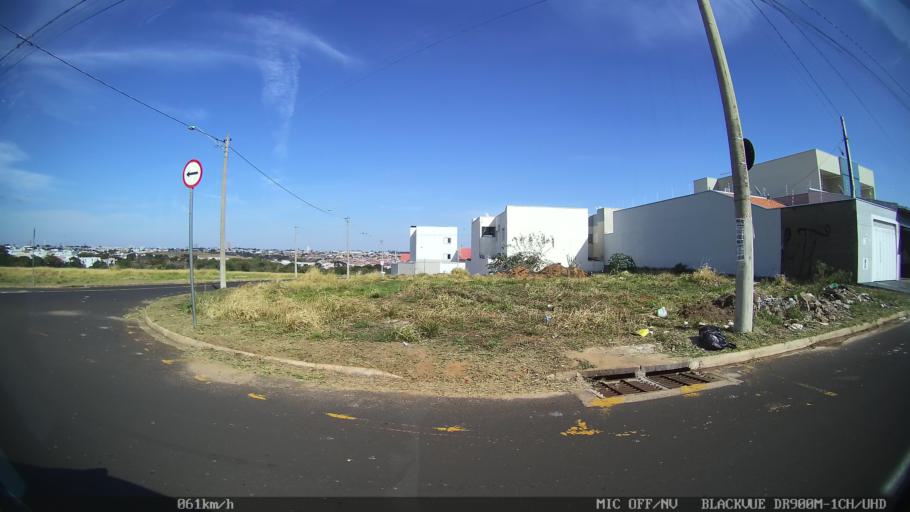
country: BR
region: Sao Paulo
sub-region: Franca
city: Franca
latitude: -20.5065
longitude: -47.4341
